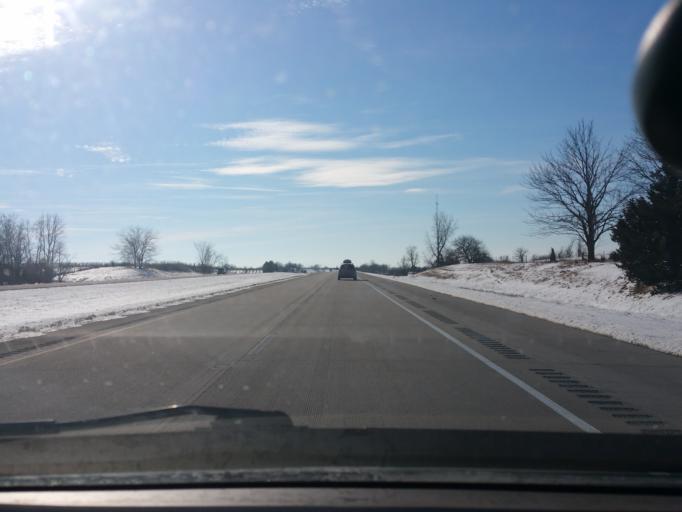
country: US
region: Iowa
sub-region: Decatur County
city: Leon
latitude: 40.7697
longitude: -93.8364
